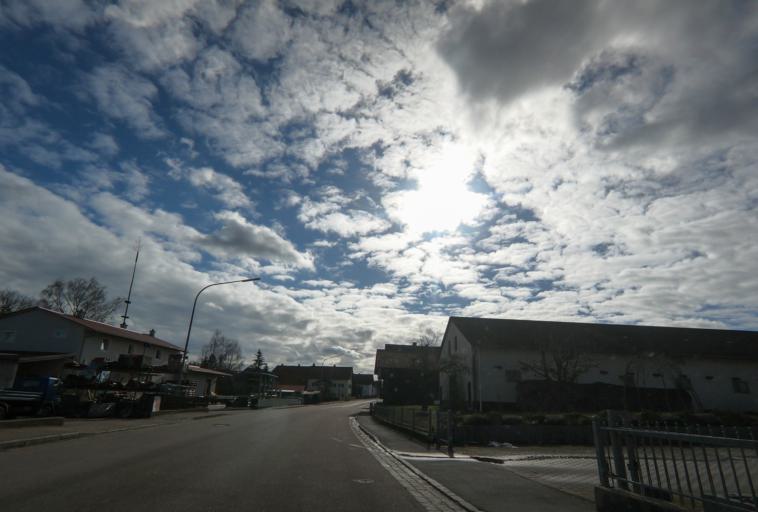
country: DE
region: Bavaria
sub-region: Upper Palatinate
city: Schierling
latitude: 48.8151
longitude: 12.1714
